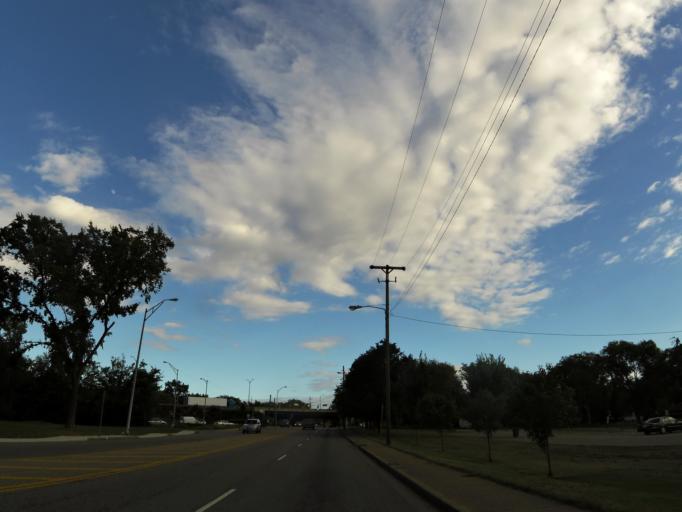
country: US
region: Tennessee
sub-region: Davidson County
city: Nashville
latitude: 36.1655
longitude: -86.8203
